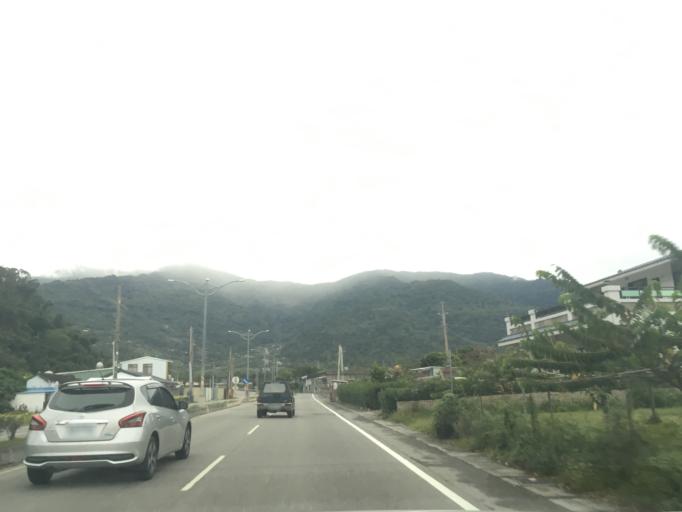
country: TW
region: Taiwan
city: Taitung City
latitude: 22.6977
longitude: 121.0430
